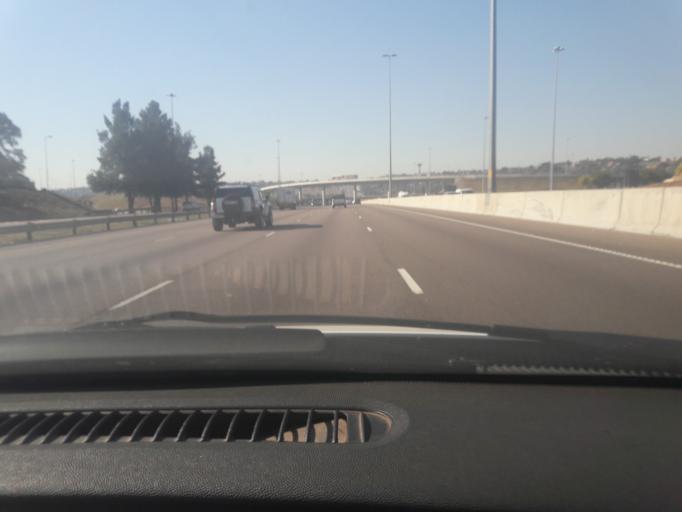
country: ZA
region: Gauteng
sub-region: City of Tshwane Metropolitan Municipality
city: Centurion
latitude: -25.8322
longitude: 28.2407
